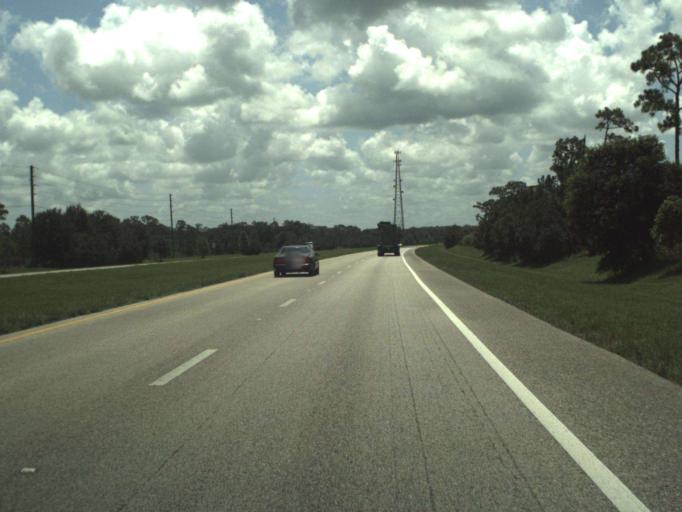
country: US
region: Florida
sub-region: Indian River County
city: Fellsmere
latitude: 27.6761
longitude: -80.8136
